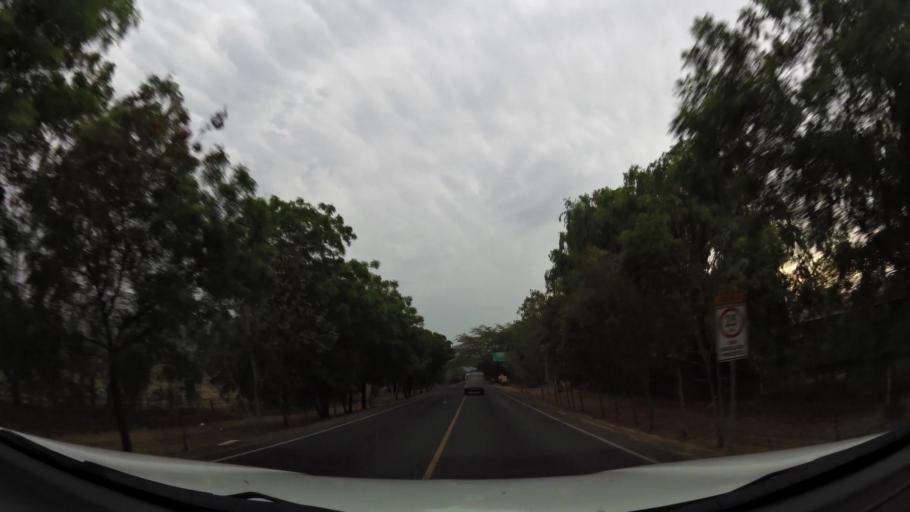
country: NI
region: Matagalpa
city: Ciudad Dario
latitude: 12.9096
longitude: -86.1757
